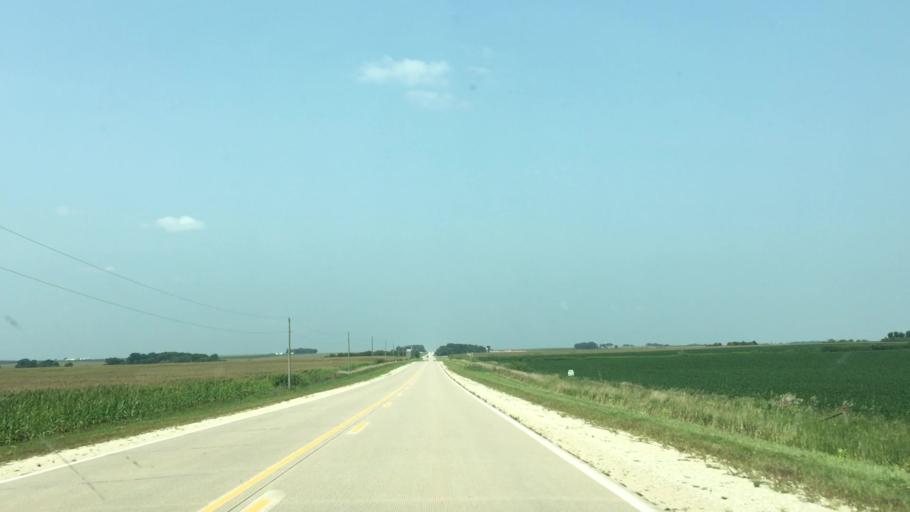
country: US
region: Iowa
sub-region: Fayette County
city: Fayette
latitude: 42.7467
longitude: -91.8041
